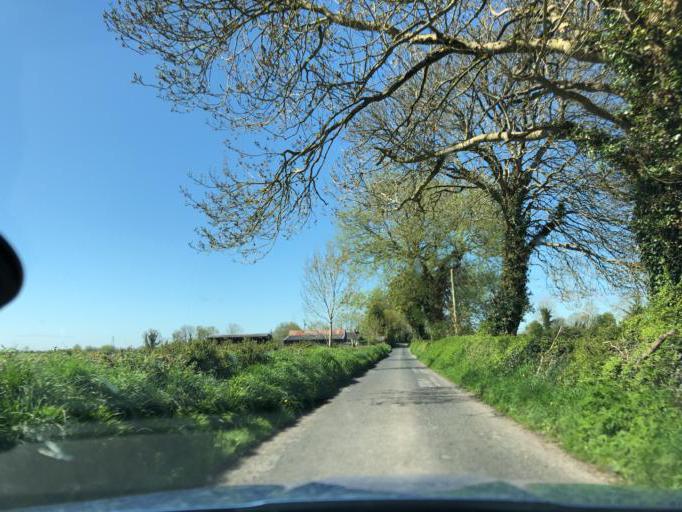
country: IE
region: Connaught
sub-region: County Galway
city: Portumna
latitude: 53.1571
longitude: -8.3076
